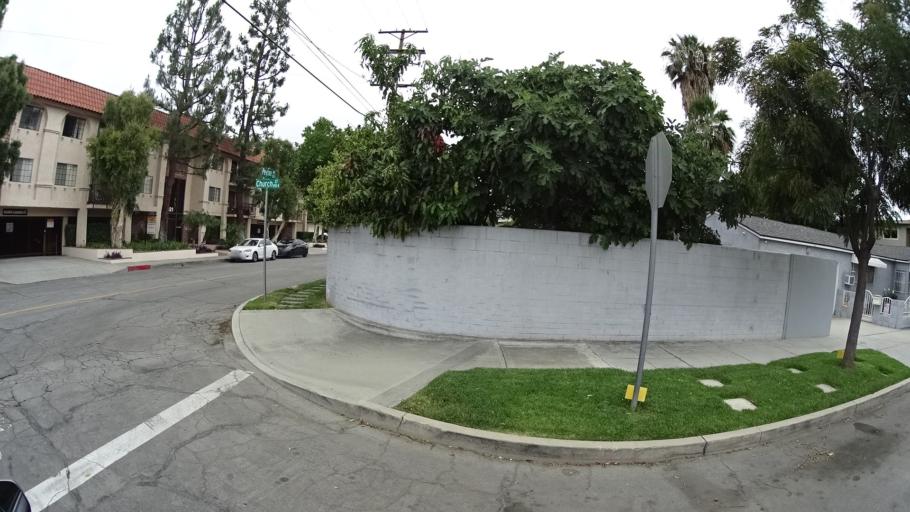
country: US
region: California
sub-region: Los Angeles County
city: Burbank
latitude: 34.1964
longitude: -118.3308
